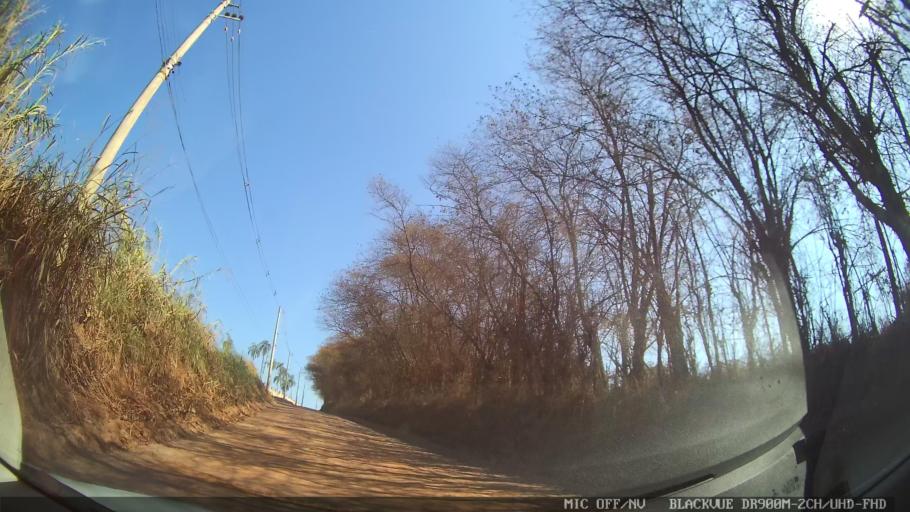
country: BR
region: Sao Paulo
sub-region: Itupeva
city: Itupeva
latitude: -23.1120
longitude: -47.0460
